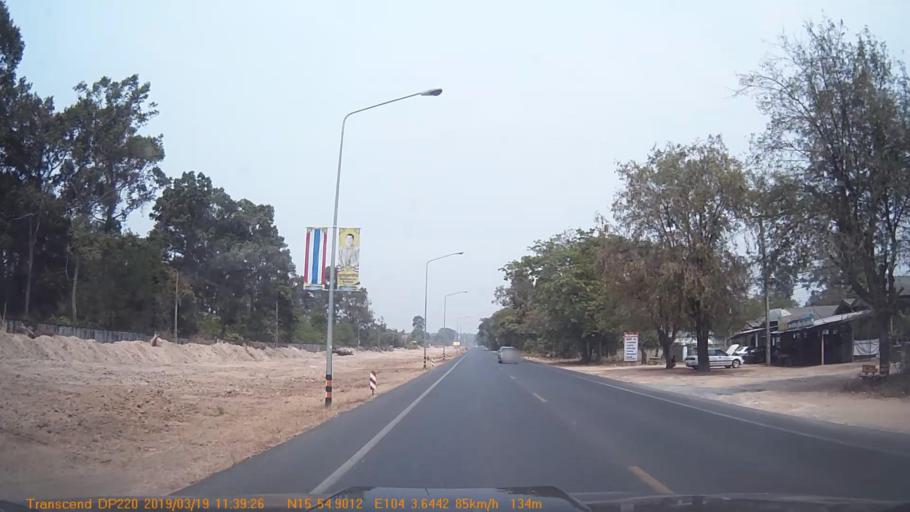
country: TH
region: Yasothon
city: Yasothon
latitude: 15.9152
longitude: 104.0606
